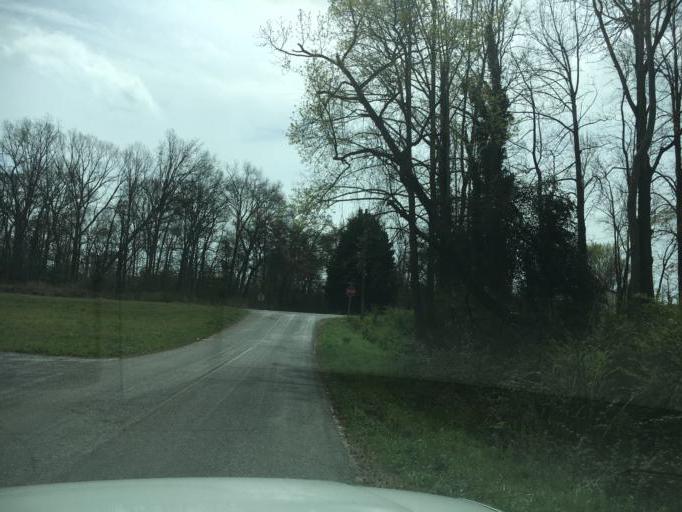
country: US
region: Georgia
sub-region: Hart County
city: Royston
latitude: 34.3580
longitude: -83.0462
